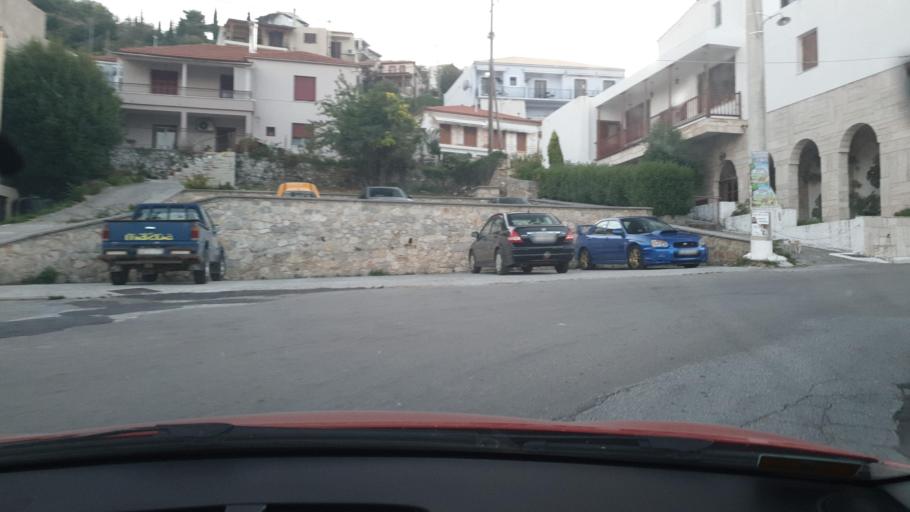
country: GR
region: Central Greece
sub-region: Nomos Evvoias
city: Kymi
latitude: 38.6311
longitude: 24.1051
